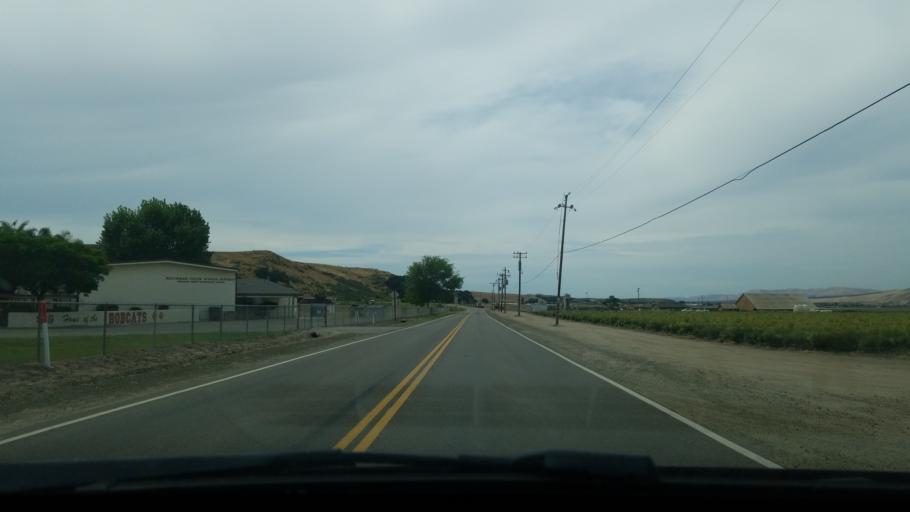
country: US
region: California
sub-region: Santa Barbara County
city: Los Alamos
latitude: 34.8667
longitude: -120.2953
